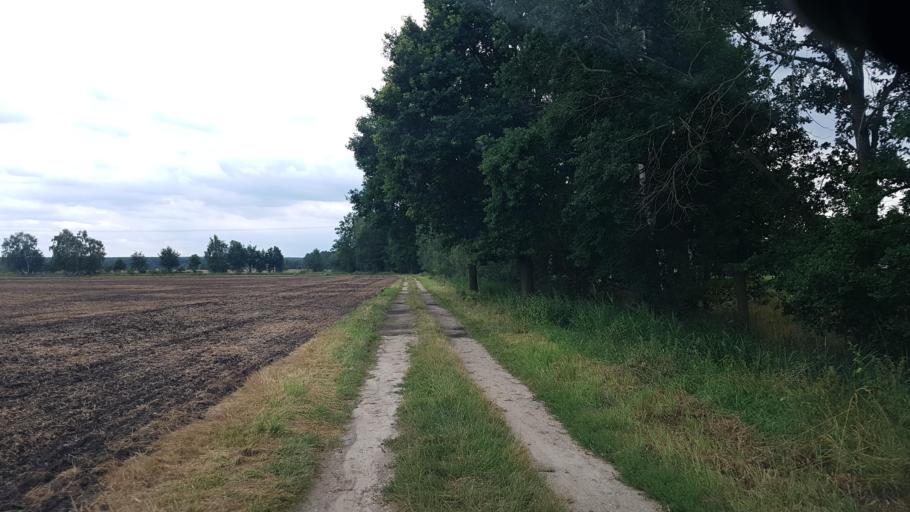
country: DE
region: Brandenburg
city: Schilda
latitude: 51.6478
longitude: 13.3939
